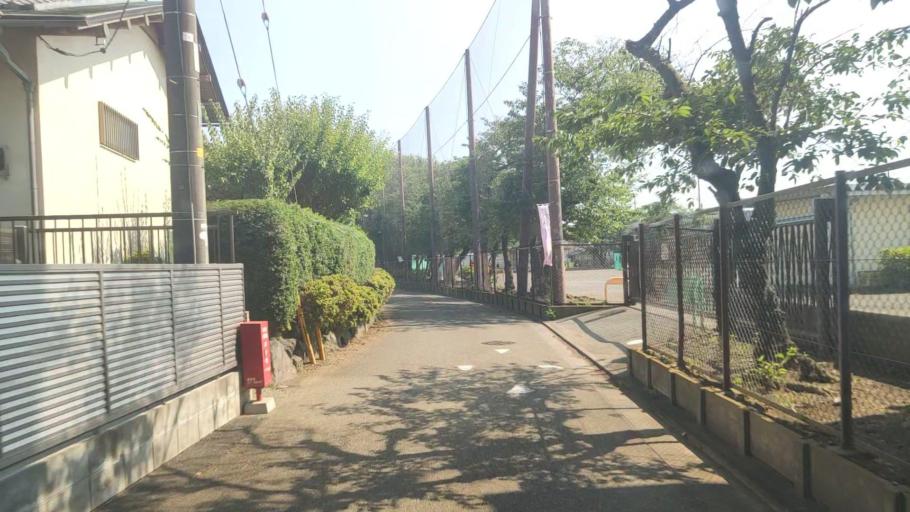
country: JP
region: Kanagawa
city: Hiratsuka
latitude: 35.3586
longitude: 139.3317
